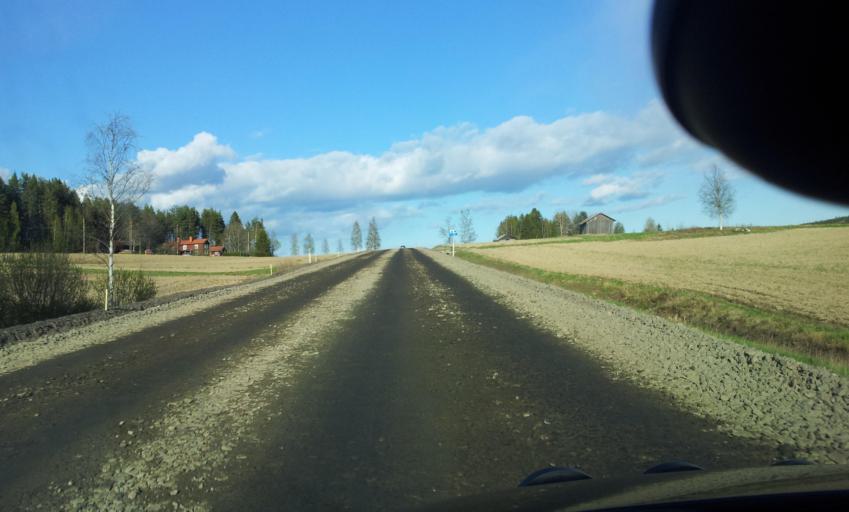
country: SE
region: Gaevleborg
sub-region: Bollnas Kommun
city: Kilafors
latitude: 61.3502
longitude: 16.6459
